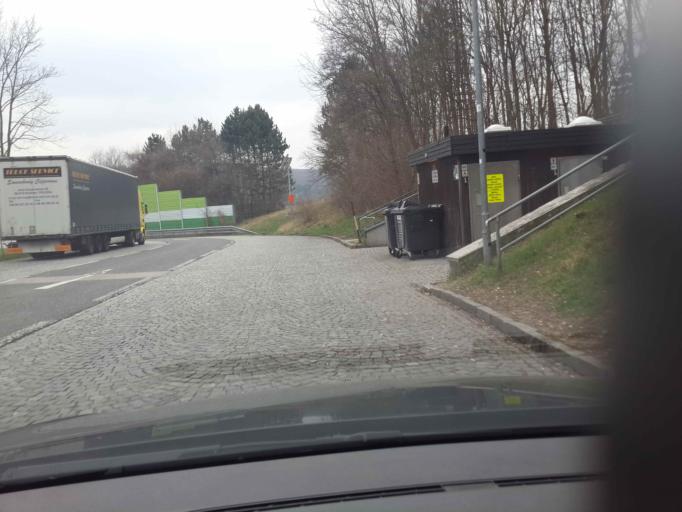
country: AT
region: Lower Austria
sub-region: Politischer Bezirk Modling
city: Gaaden
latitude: 48.0730
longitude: 16.2026
